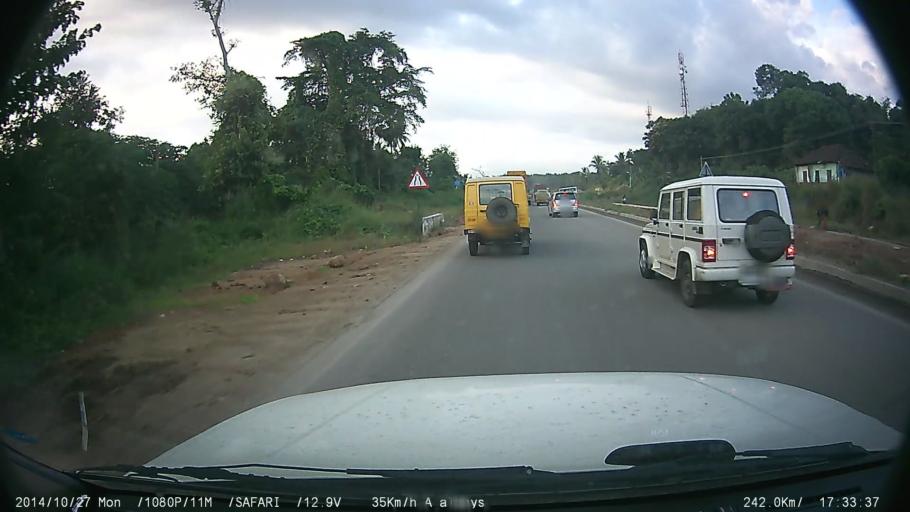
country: IN
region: Kerala
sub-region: Palakkad district
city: Palakkad
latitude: 10.6818
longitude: 76.5786
